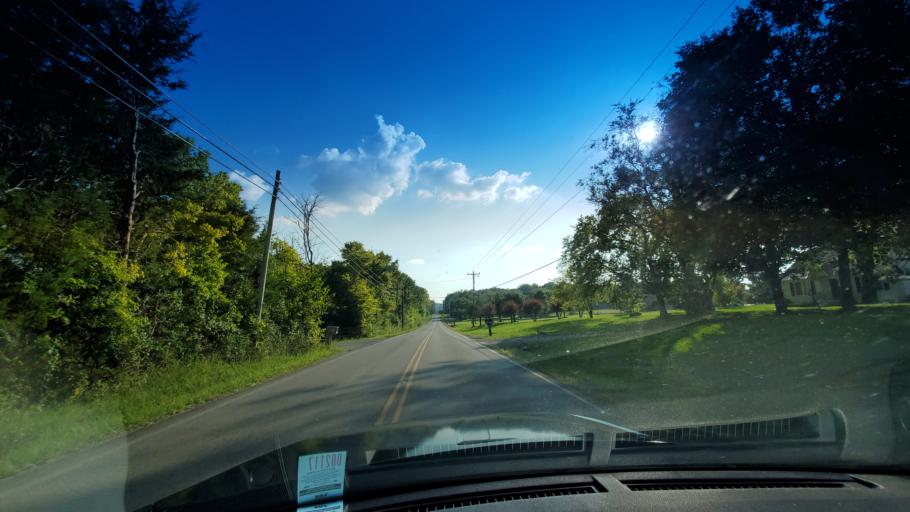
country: US
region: Tennessee
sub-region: Wilson County
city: Lebanon
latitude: 36.1729
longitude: -86.3549
